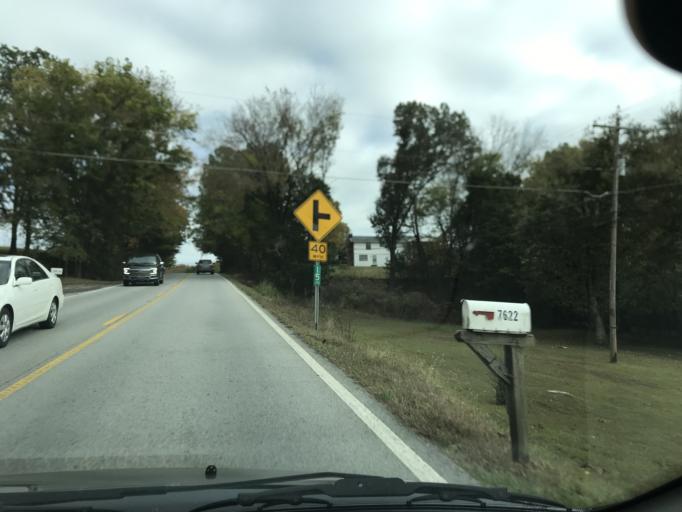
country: US
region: Tennessee
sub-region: Hamilton County
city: Lakesite
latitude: 35.1799
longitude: -85.0515
